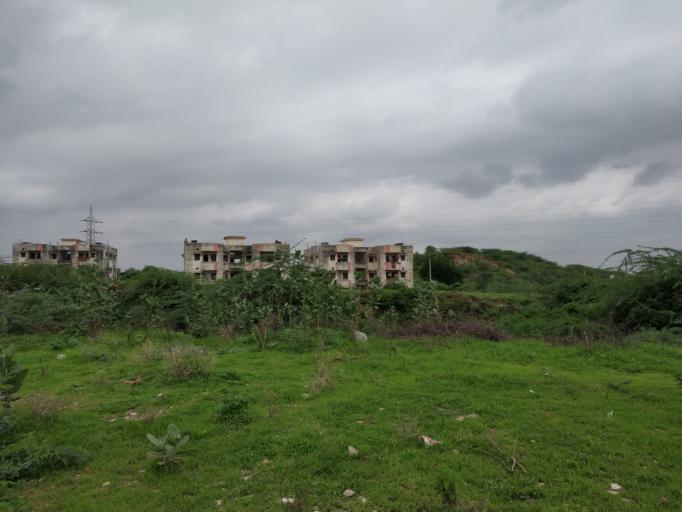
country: IN
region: Rajasthan
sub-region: Udaipur
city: Udaipur
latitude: 24.5914
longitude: 73.6543
